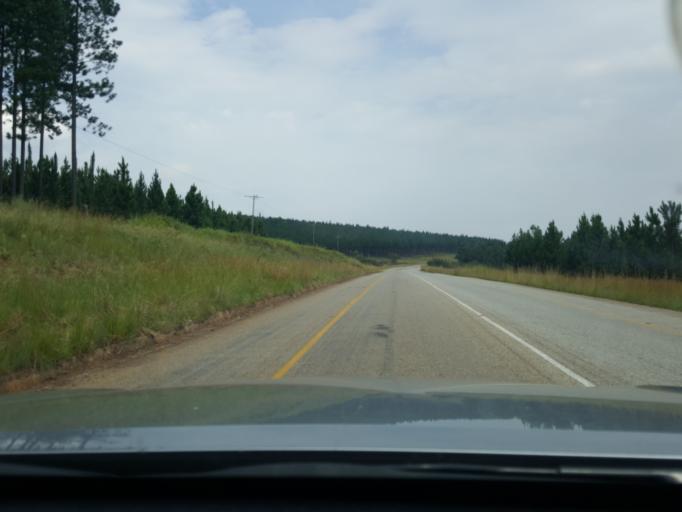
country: ZA
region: Mpumalanga
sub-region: Ehlanzeni District
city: White River
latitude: -25.2491
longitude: 30.9615
